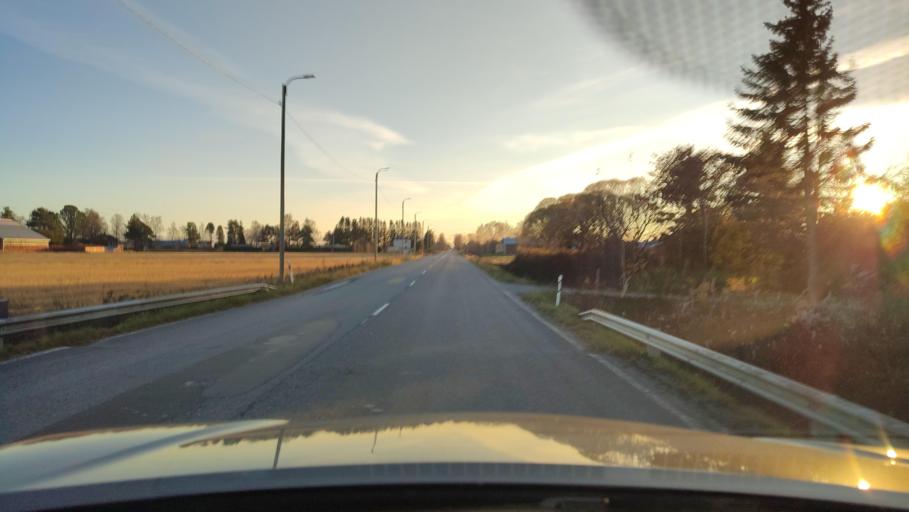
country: FI
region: Ostrobothnia
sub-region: Sydosterbotten
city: Naerpes
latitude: 62.5385
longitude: 21.3898
